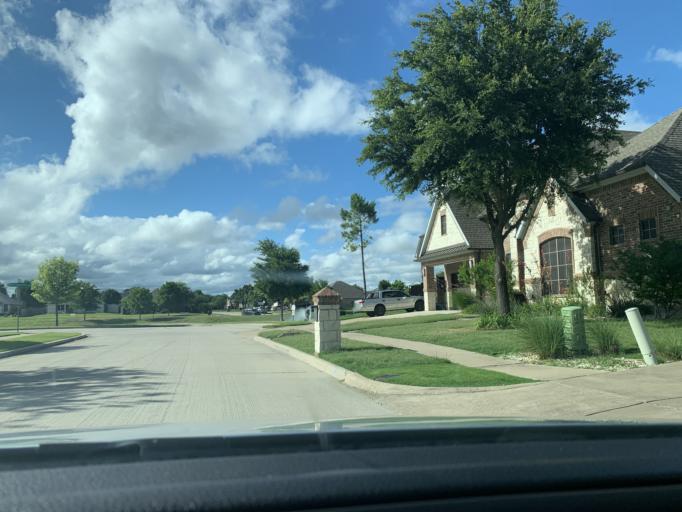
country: US
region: Texas
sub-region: Dallas County
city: Cedar Hill
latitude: 32.6413
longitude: -97.0418
